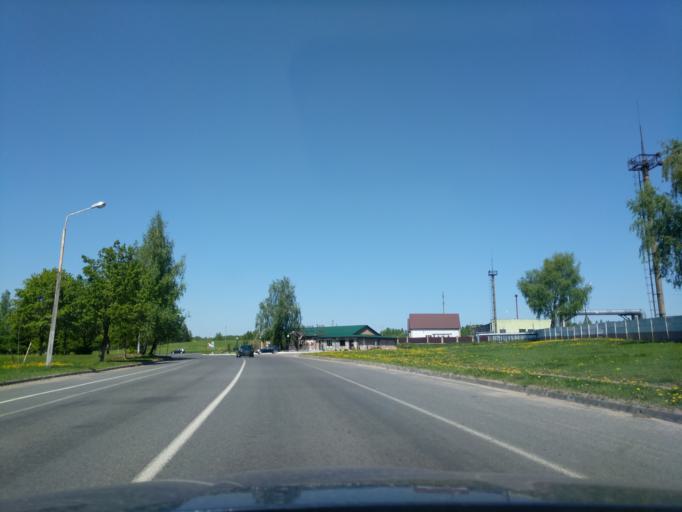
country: BY
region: Minsk
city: Myadzyel
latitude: 54.8844
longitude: 26.9378
